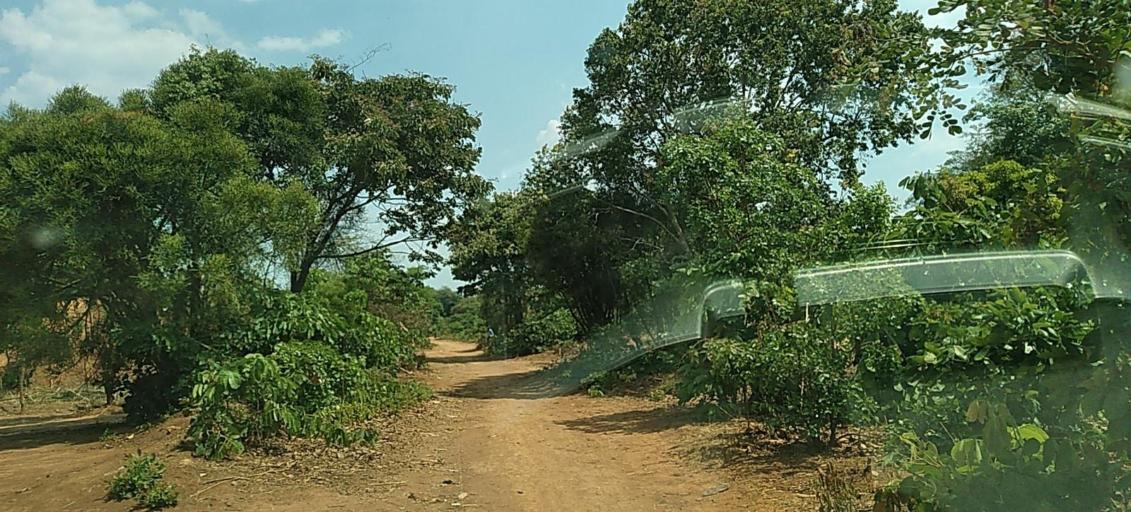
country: CD
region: Katanga
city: Kipushi
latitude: -12.0327
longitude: 27.4361
